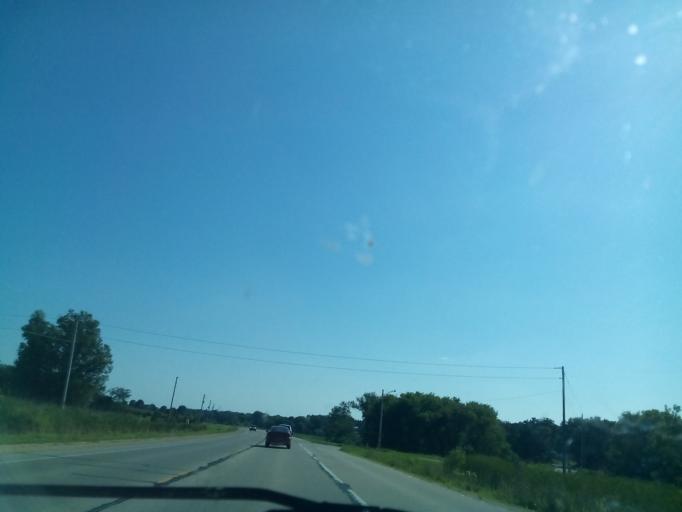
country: US
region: Wisconsin
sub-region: Green County
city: New Glarus
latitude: 42.8433
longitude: -89.6330
